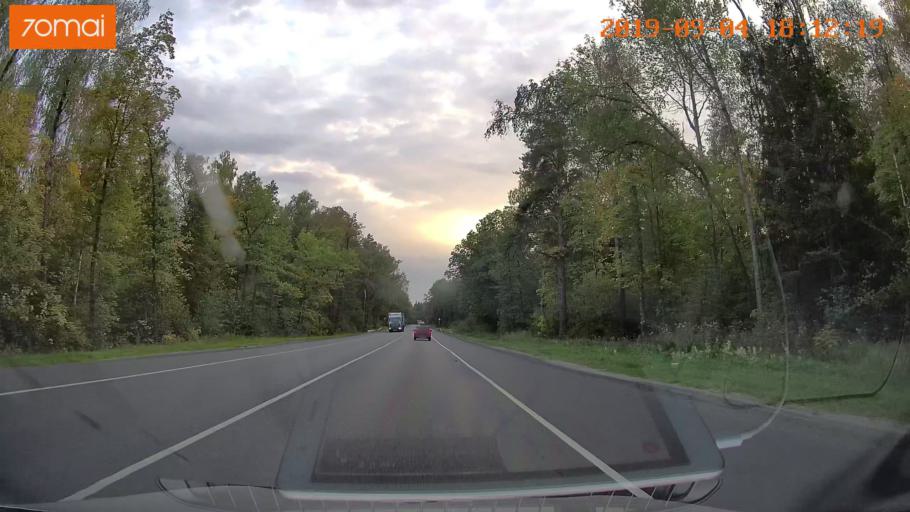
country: RU
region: Moskovskaya
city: Lopatinskiy
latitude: 55.3712
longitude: 38.7437
